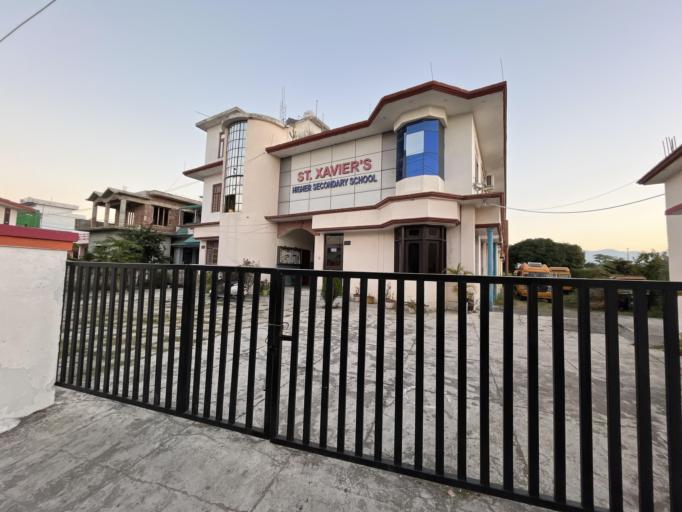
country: IN
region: Uttarakhand
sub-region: Naini Tal
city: Haldwani
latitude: 29.1985
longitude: 79.4839
